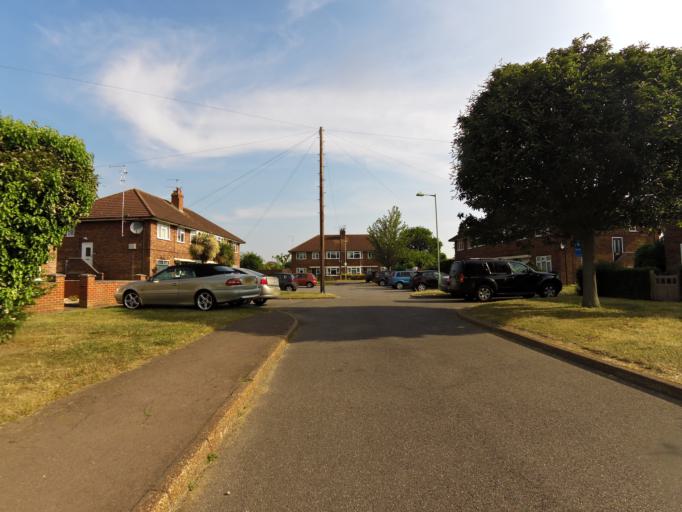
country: GB
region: England
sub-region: Suffolk
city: Kesgrave
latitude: 52.0561
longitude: 1.2323
